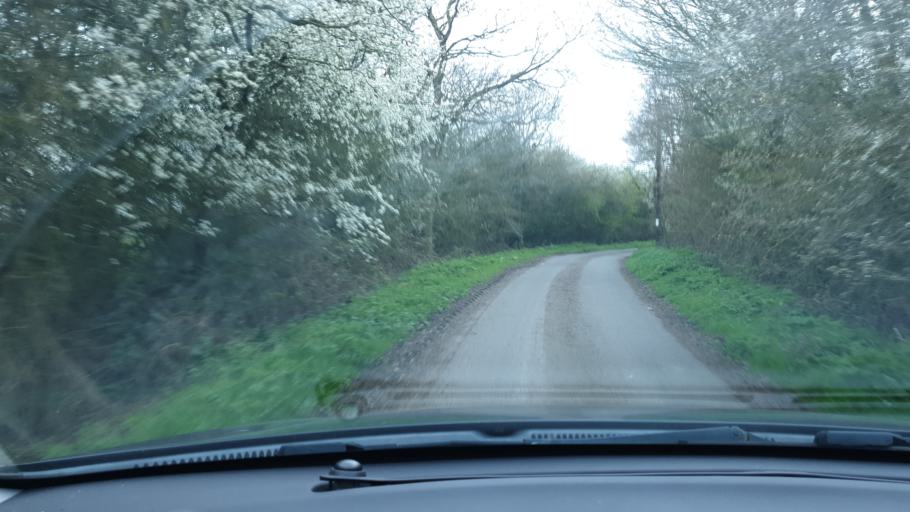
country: GB
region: England
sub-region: Essex
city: Little Clacton
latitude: 51.8914
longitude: 1.1306
